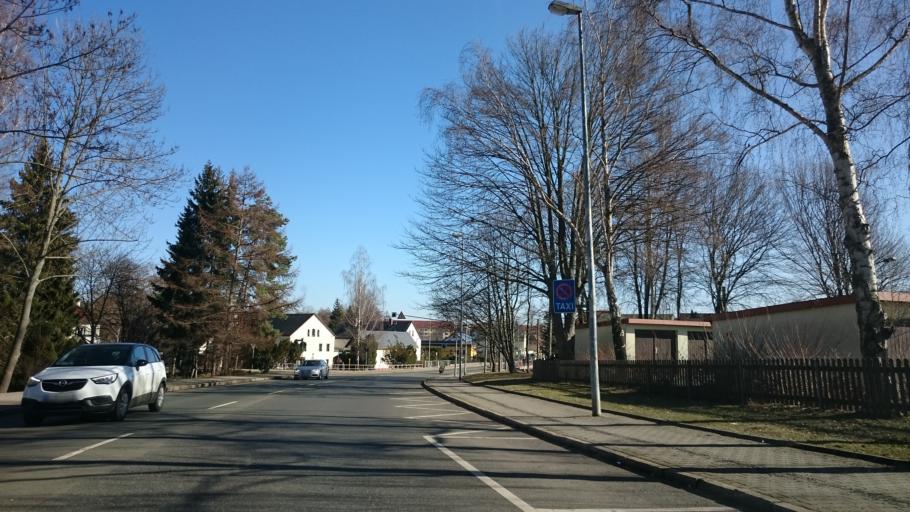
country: DE
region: Saxony
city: Lichtentanne
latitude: 50.7227
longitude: 12.4442
